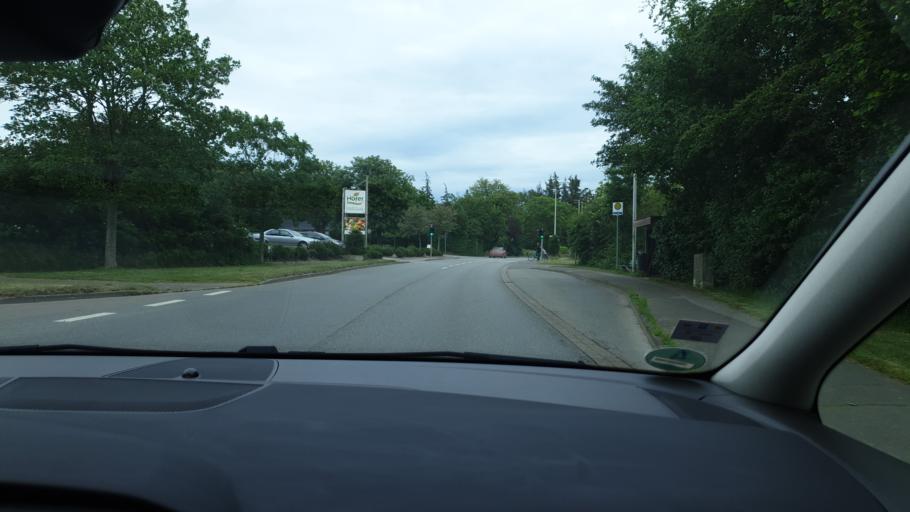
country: DE
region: Schleswig-Holstein
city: Schobull
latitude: 54.5078
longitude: 9.0060
